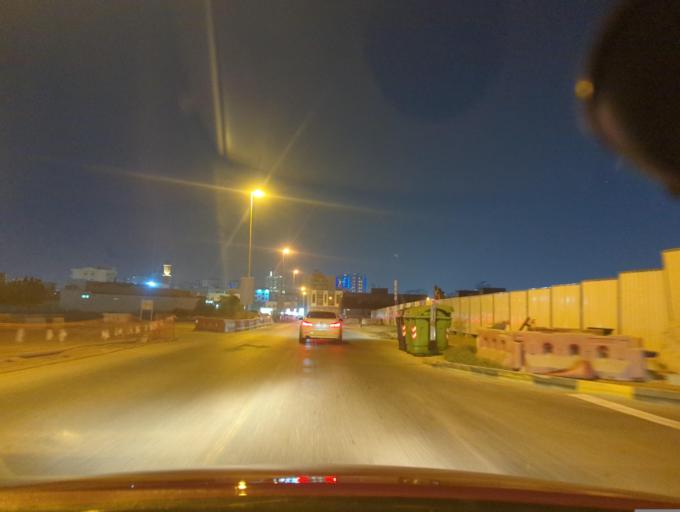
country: AE
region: Ajman
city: Ajman
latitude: 25.3795
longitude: 55.4458
